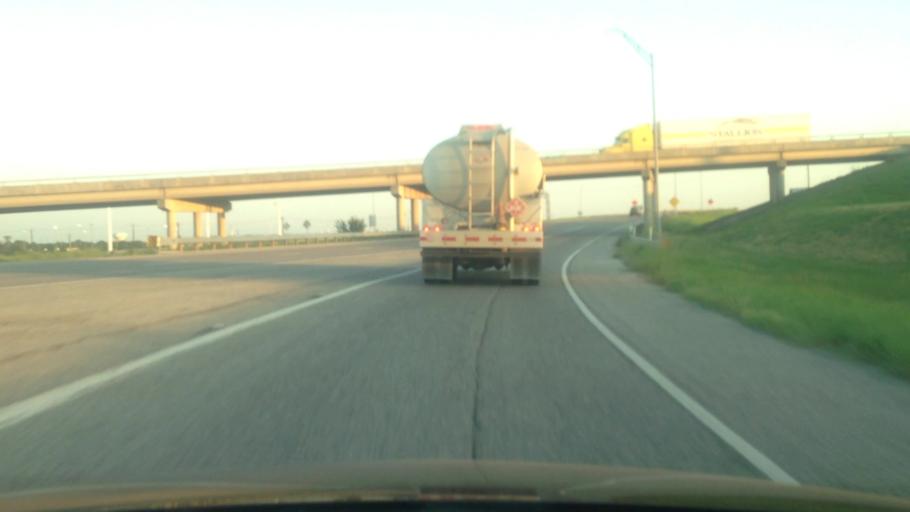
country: US
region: Texas
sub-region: Denton County
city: Denton
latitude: 33.2064
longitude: -97.1643
